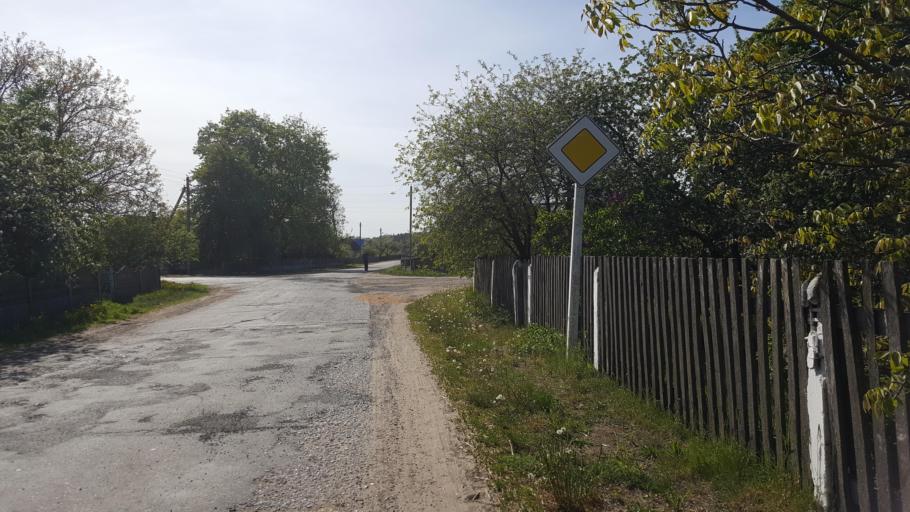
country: BY
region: Brest
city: Zhabinka
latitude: 52.3159
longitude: 23.9951
